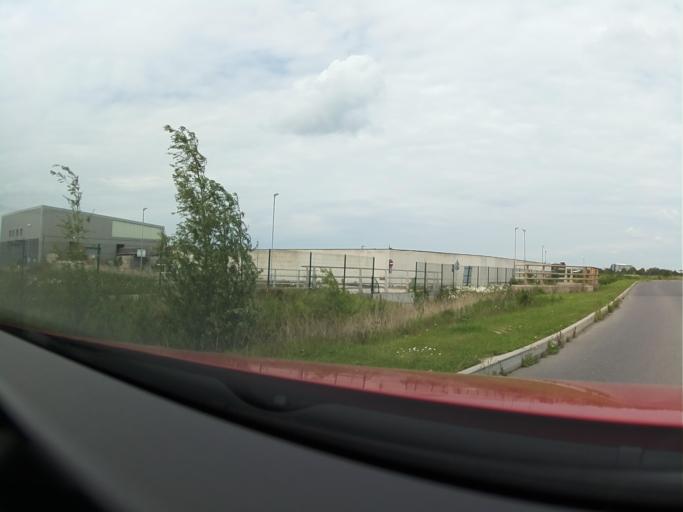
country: GB
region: England
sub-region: South Gloucestershire
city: Severn Beach
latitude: 51.5401
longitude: -2.6660
